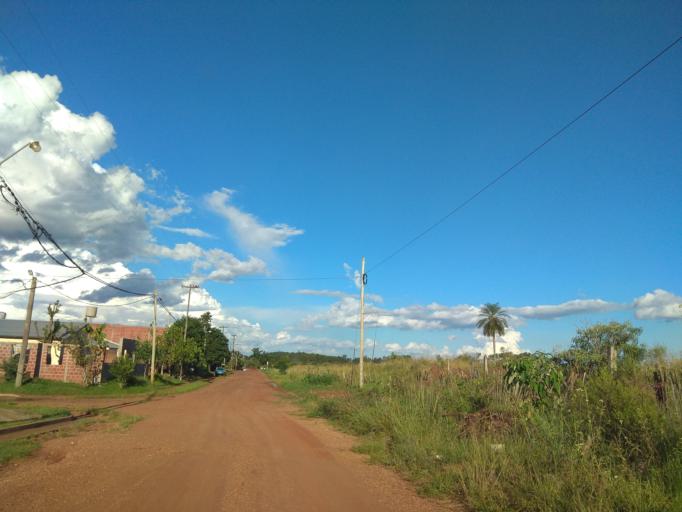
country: AR
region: Misiones
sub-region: Departamento de Candelaria
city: Candelaria
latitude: -27.4799
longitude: -55.7505
